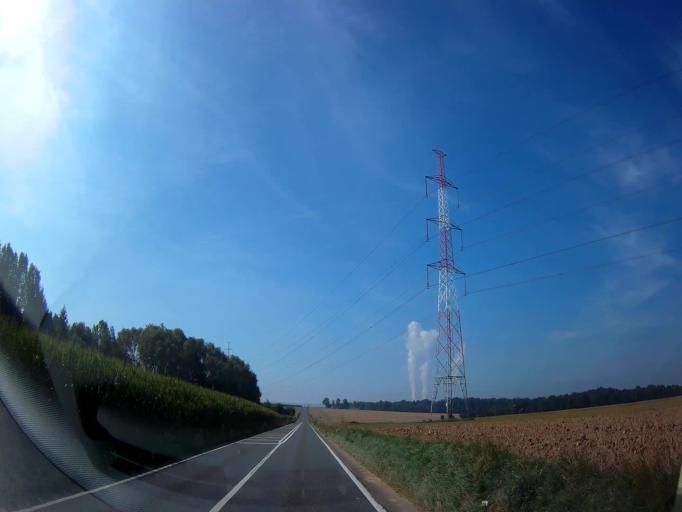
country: BE
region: Wallonia
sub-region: Province de Liege
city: Verlaine
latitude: 50.5862
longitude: 5.3356
